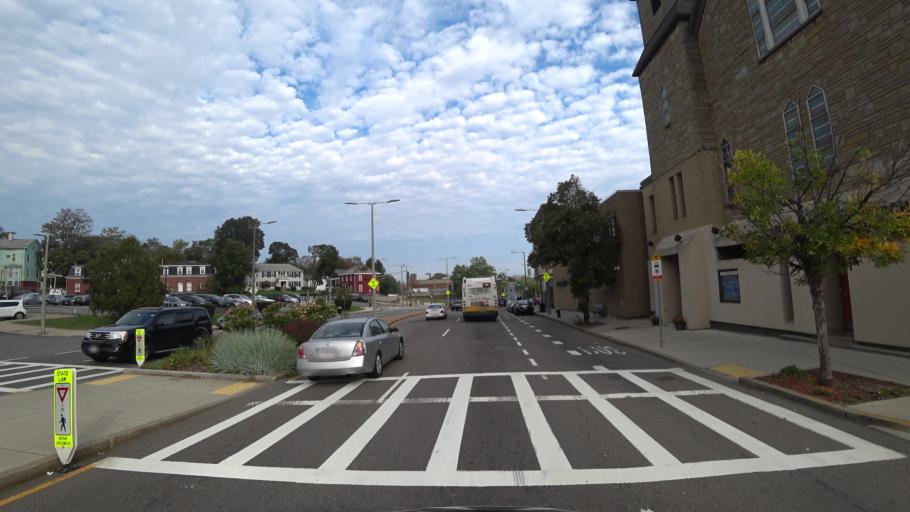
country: US
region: Massachusetts
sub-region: Suffolk County
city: South Boston
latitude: 42.3252
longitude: -71.0831
